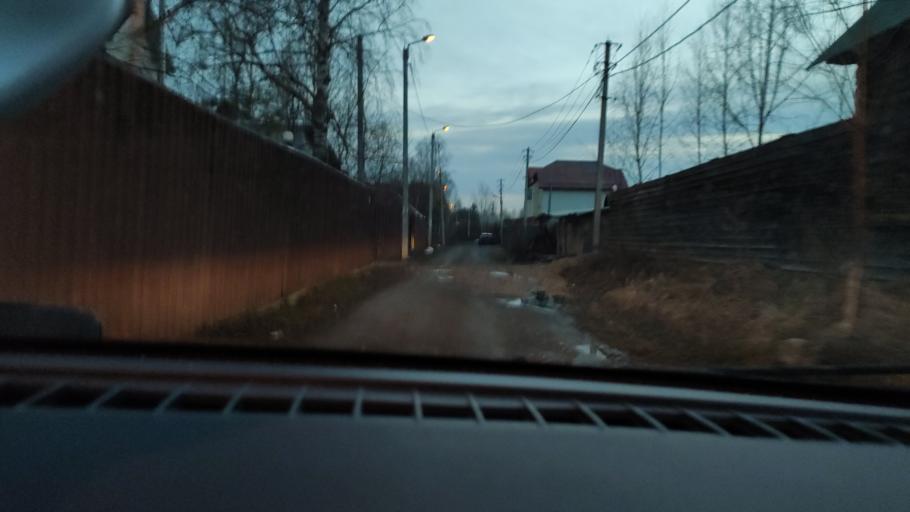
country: RU
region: Perm
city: Perm
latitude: 58.0332
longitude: 56.2490
